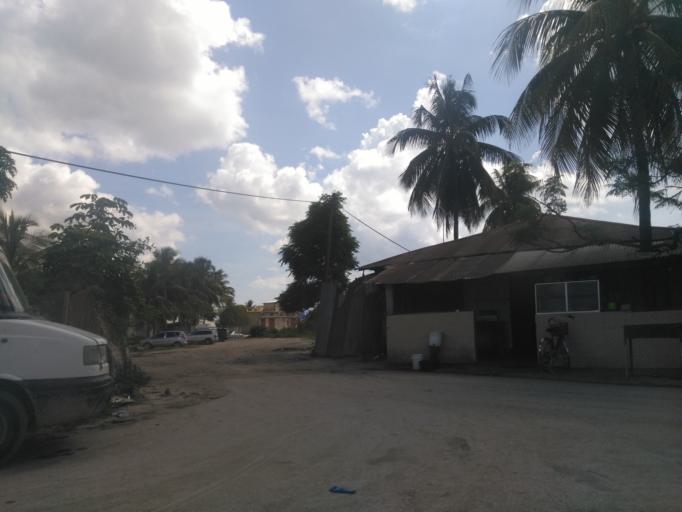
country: TZ
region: Zanzibar Urban/West
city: Zanzibar
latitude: -6.1708
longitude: 39.2113
